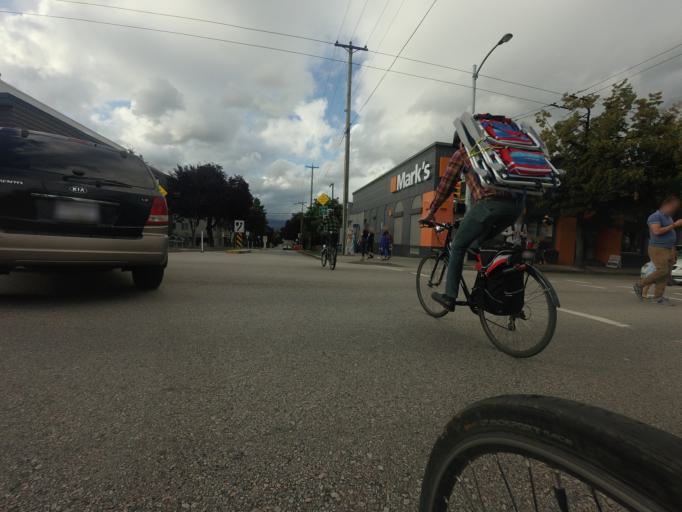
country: CA
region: British Columbia
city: West End
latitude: 49.2680
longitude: -123.1479
